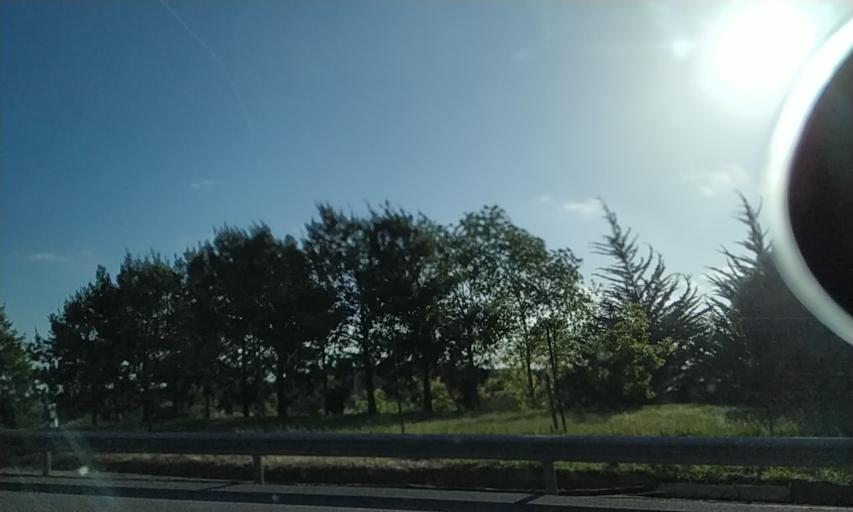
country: PT
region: Lisbon
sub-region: Torres Vedras
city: Torres Vedras
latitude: 39.0581
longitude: -9.2395
